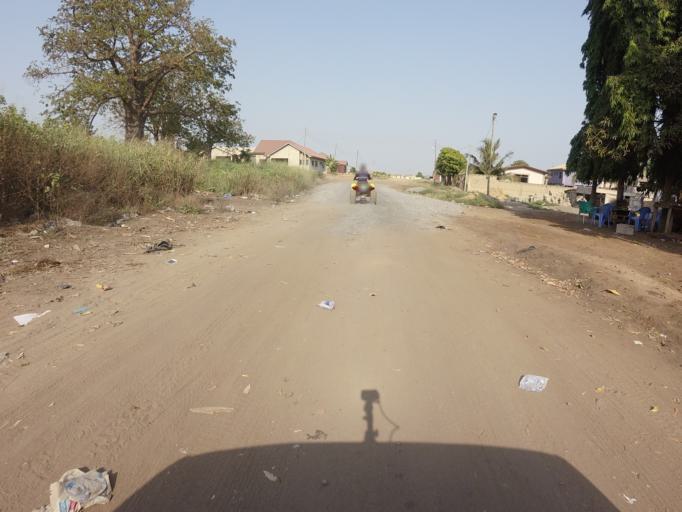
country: GH
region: Greater Accra
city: Tema
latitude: 5.7014
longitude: 0.0606
